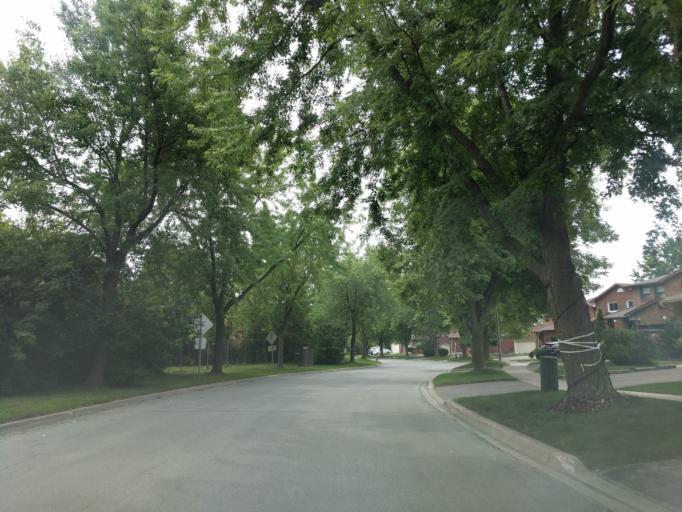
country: CA
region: Ontario
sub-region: York
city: Richmond Hill
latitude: 43.8689
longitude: -79.4193
